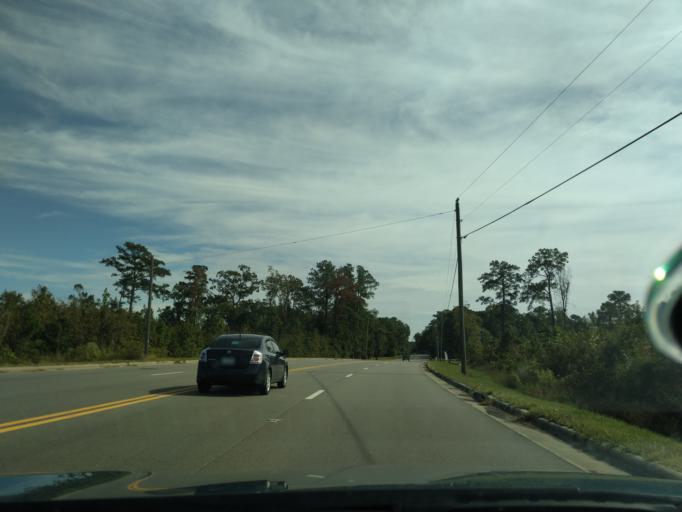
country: US
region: North Carolina
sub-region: Beaufort County
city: River Road
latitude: 35.5274
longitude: -77.0123
